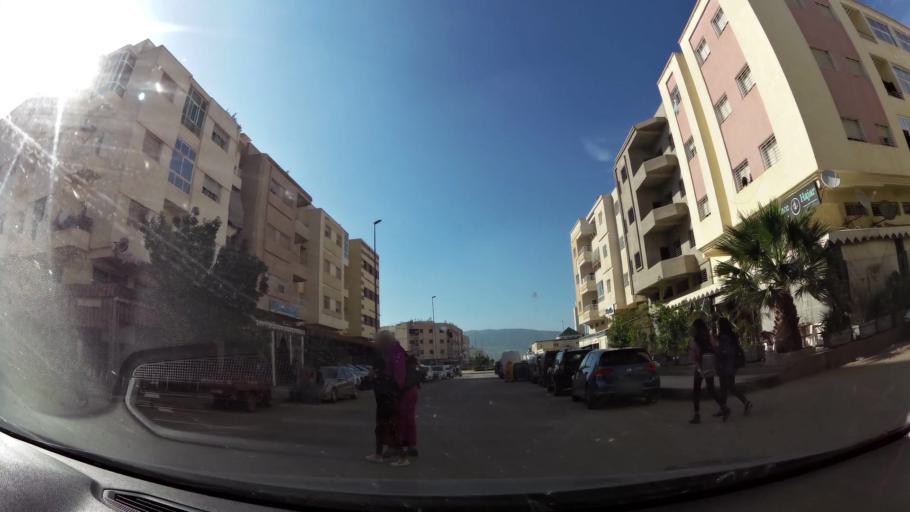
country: MA
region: Fes-Boulemane
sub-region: Fes
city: Fes
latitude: 34.0213
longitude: -5.0307
